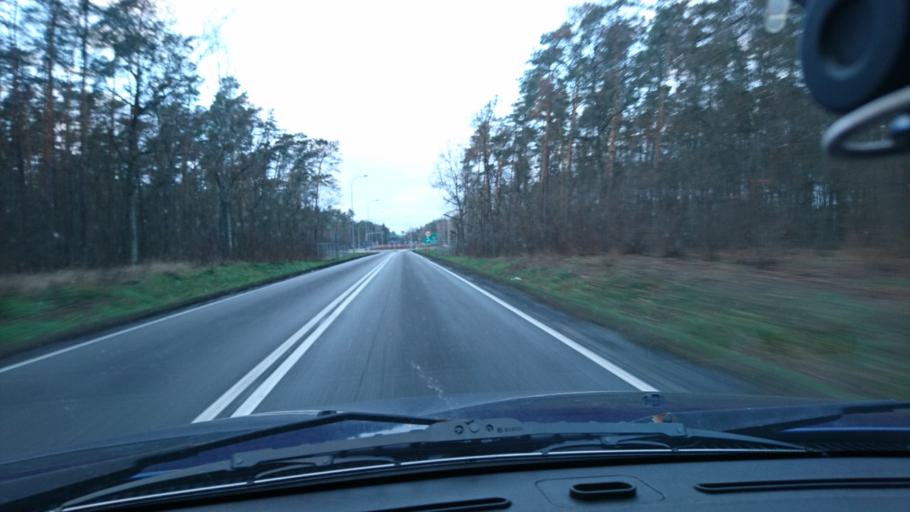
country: PL
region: Greater Poland Voivodeship
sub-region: Powiat kepinski
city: Kepno
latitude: 51.3290
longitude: 17.9604
